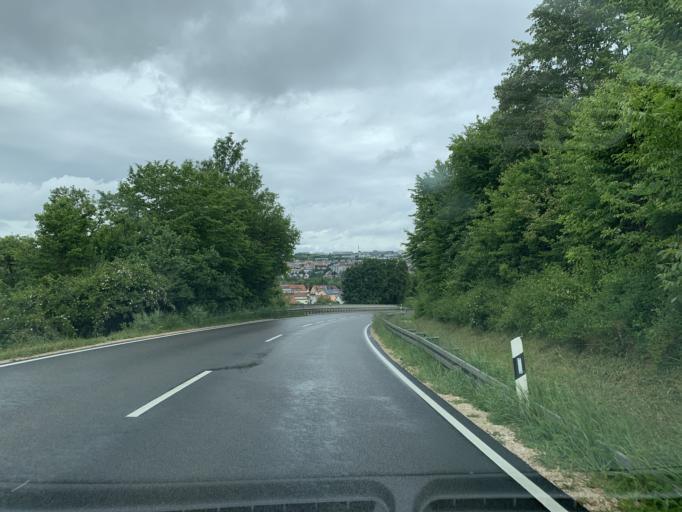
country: DE
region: Baden-Wuerttemberg
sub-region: Tuebingen Region
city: Ulm
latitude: 48.3974
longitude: 9.9396
